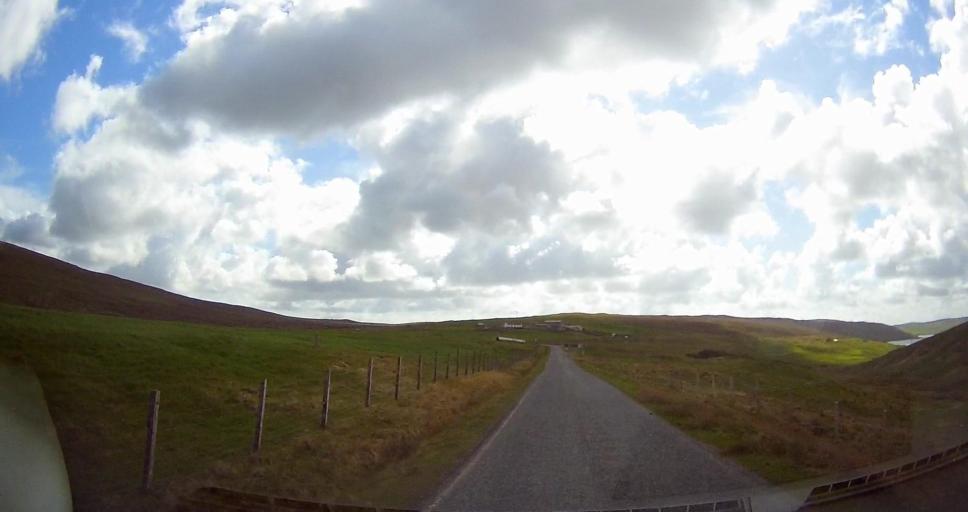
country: GB
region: Scotland
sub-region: Shetland Islands
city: Lerwick
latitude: 60.5141
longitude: -1.3829
